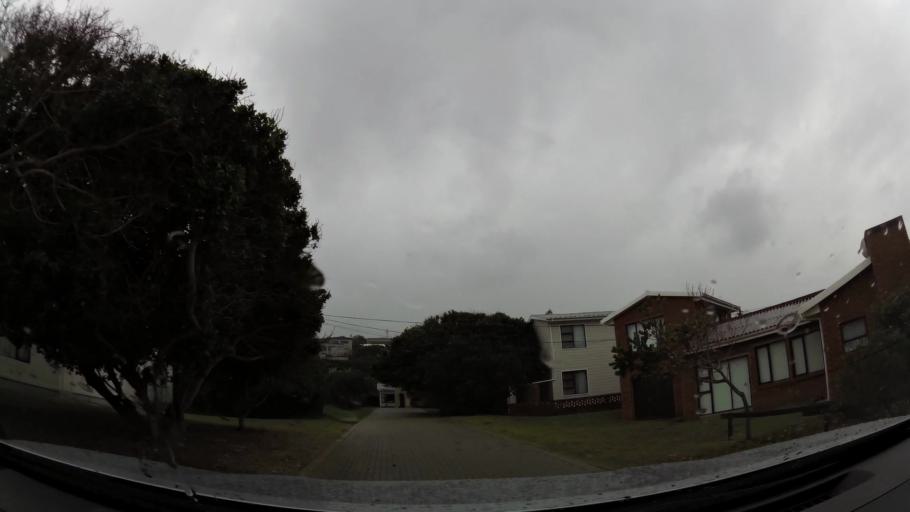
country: ZA
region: Western Cape
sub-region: Eden District Municipality
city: Mossel Bay
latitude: -34.0515
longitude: 22.2692
